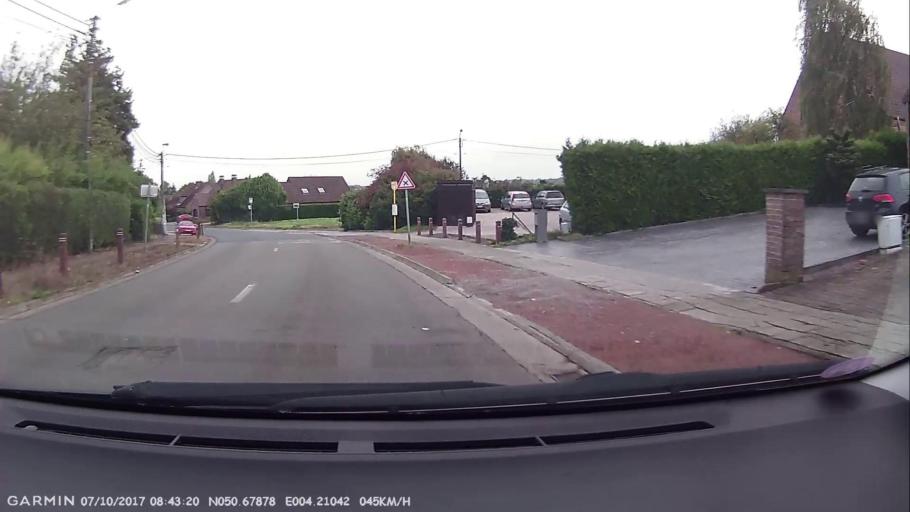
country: BE
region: Wallonia
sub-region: Province du Brabant Wallon
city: Tubize
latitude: 50.6787
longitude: 4.2105
